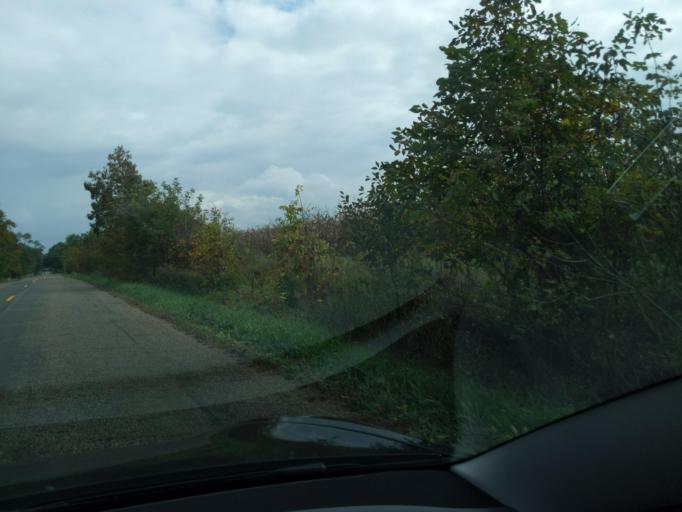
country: US
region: Michigan
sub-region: Eaton County
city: Eaton Rapids
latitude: 42.4656
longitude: -84.6045
